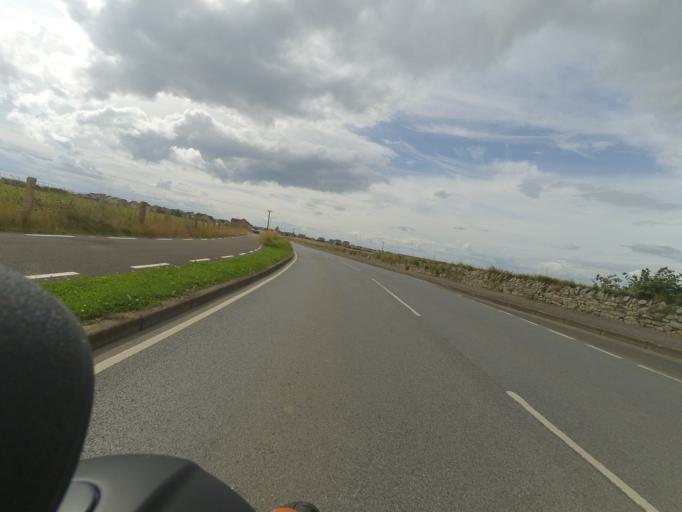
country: GB
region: Scotland
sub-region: Fife
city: Anstruther
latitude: 56.2323
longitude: -2.6890
